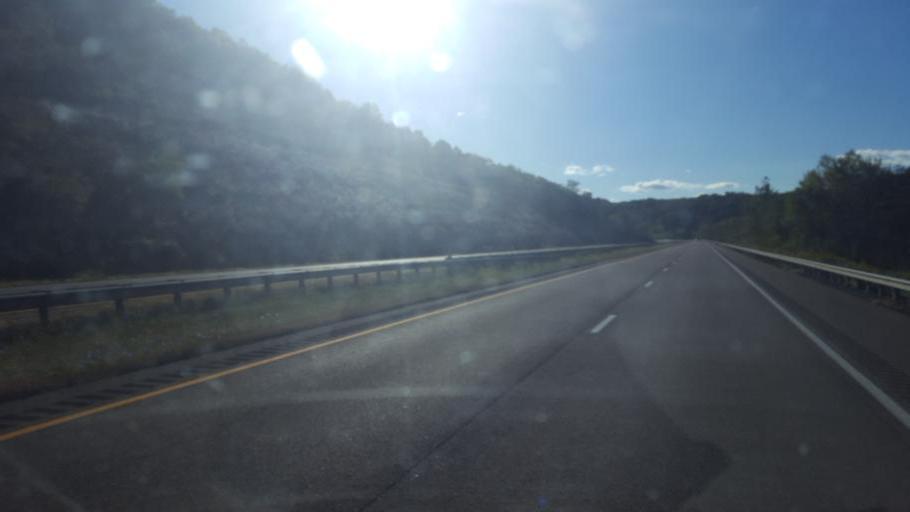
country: US
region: Maryland
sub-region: Allegany County
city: Cumberland
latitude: 39.6869
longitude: -78.4994
